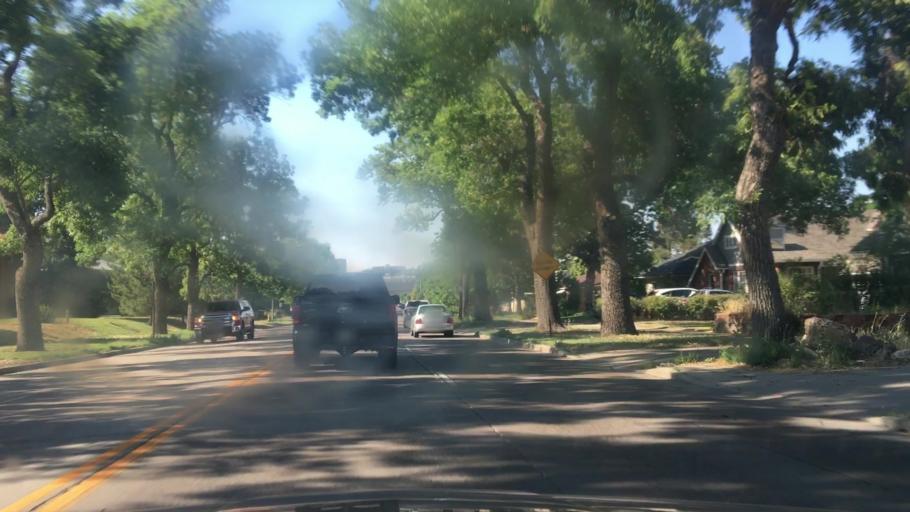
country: US
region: Colorado
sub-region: Arapahoe County
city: Glendale
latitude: 39.6886
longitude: -104.9594
